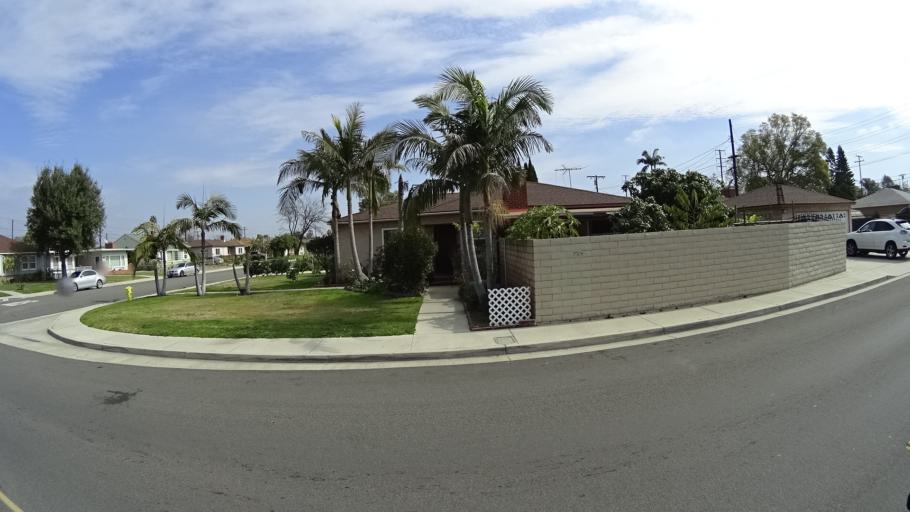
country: US
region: California
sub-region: Orange County
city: Anaheim
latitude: 33.8429
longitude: -117.9261
